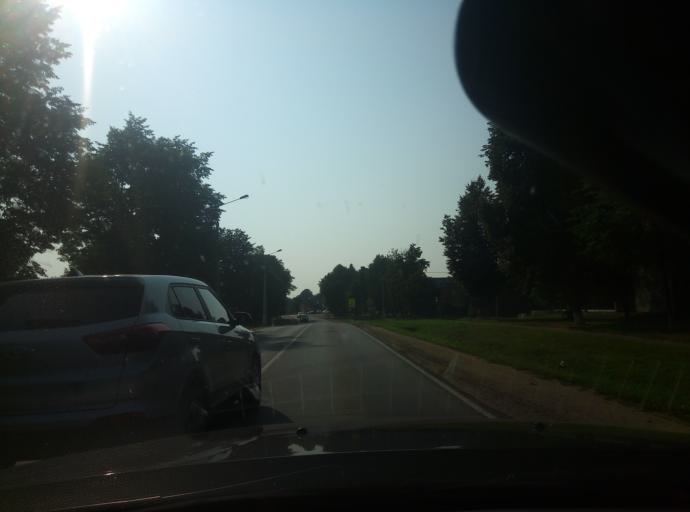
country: RU
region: Kaluga
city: Zhukovo
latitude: 55.0378
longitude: 36.7349
